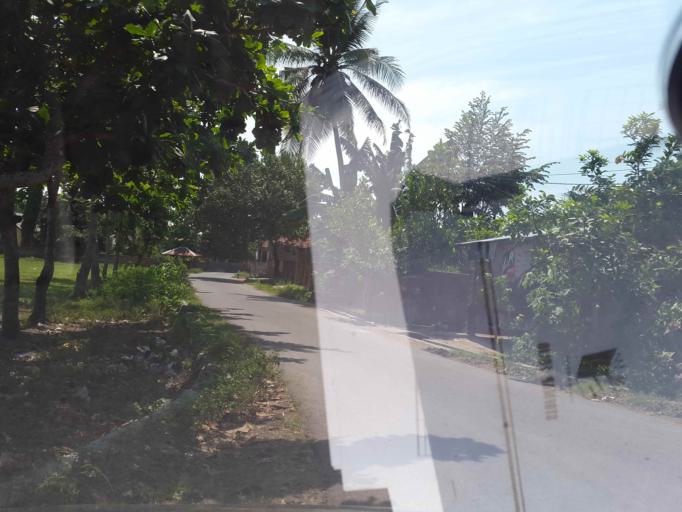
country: ID
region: West Nusa Tenggara
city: Karangkebon Timur
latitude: -8.6758
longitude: 116.0864
